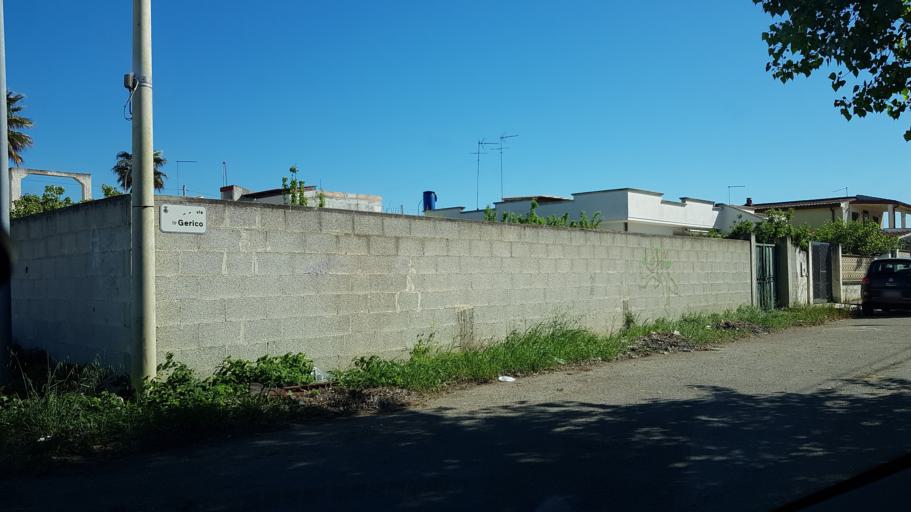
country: IT
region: Apulia
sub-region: Provincia di Brindisi
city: Torchiarolo
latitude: 40.5287
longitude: 18.0744
